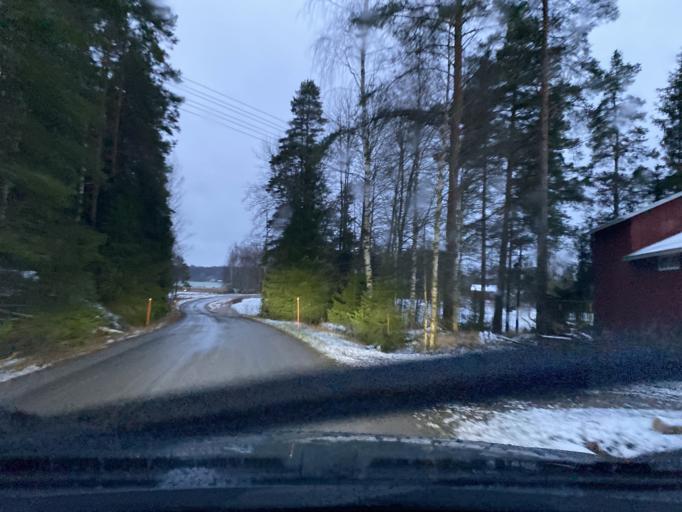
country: FI
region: Pirkanmaa
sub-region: Lounais-Pirkanmaa
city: Punkalaidun
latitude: 61.1428
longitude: 22.9650
